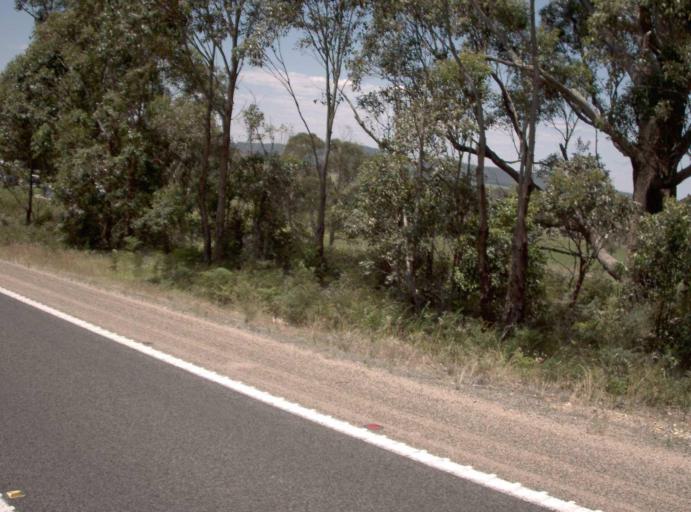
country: AU
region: Victoria
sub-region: East Gippsland
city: Lakes Entrance
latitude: -37.7059
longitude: 148.5040
